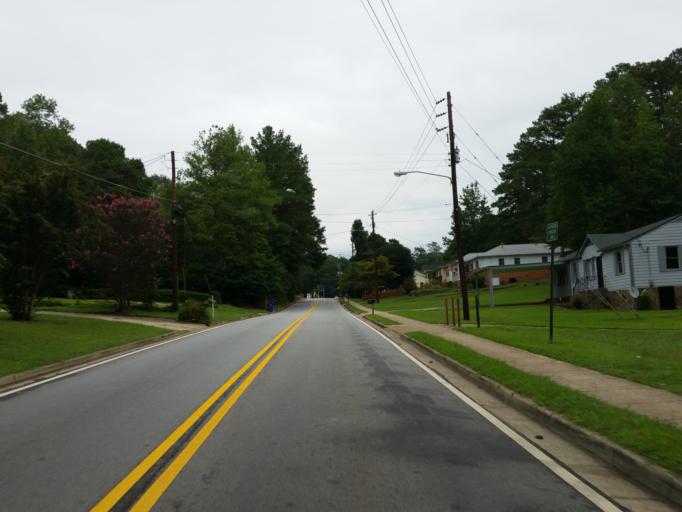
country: US
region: Georgia
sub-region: Cobb County
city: Austell
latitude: 33.8267
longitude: -84.6180
